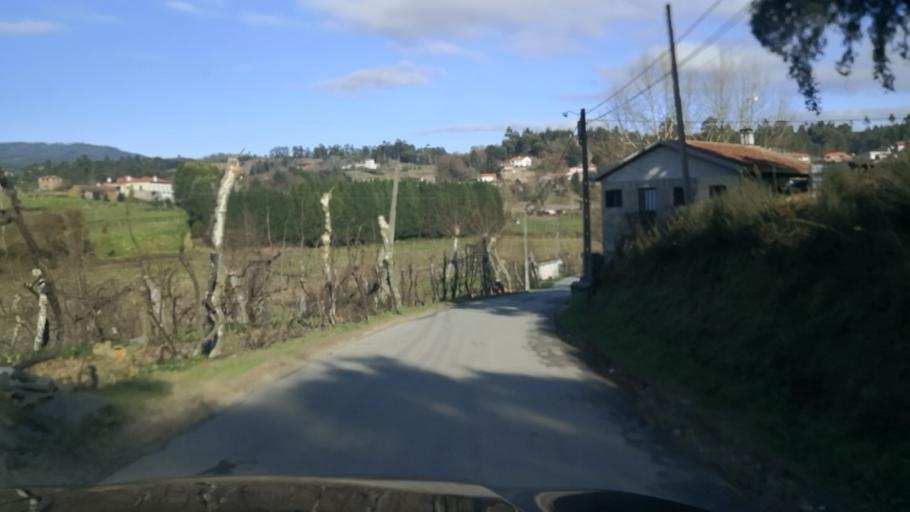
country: PT
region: Vila Real
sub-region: Mondim de Basto
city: Mondim de Basto
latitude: 41.4116
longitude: -7.9806
